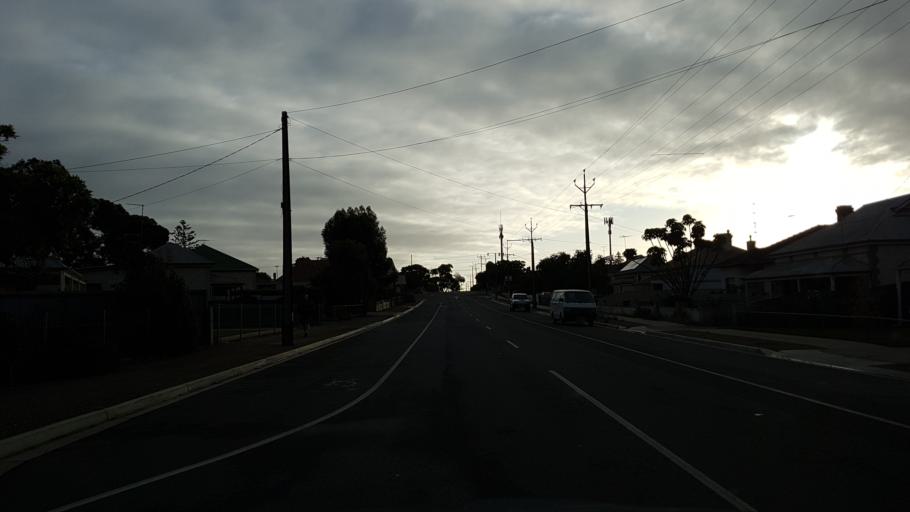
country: AU
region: South Australia
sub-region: Murray Bridge
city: Murray Bridge
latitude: -35.1205
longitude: 139.2689
